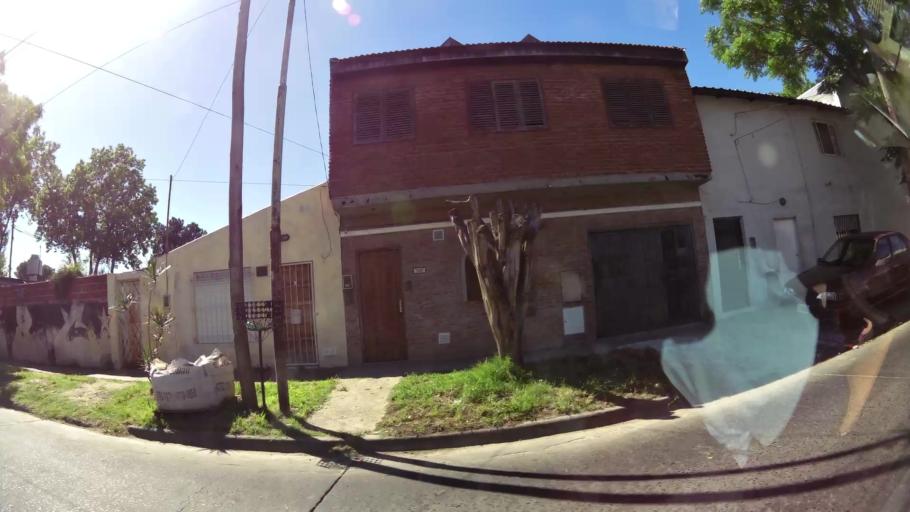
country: AR
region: Buenos Aires
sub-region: Partido de General San Martin
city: General San Martin
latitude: -34.5436
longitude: -58.5338
